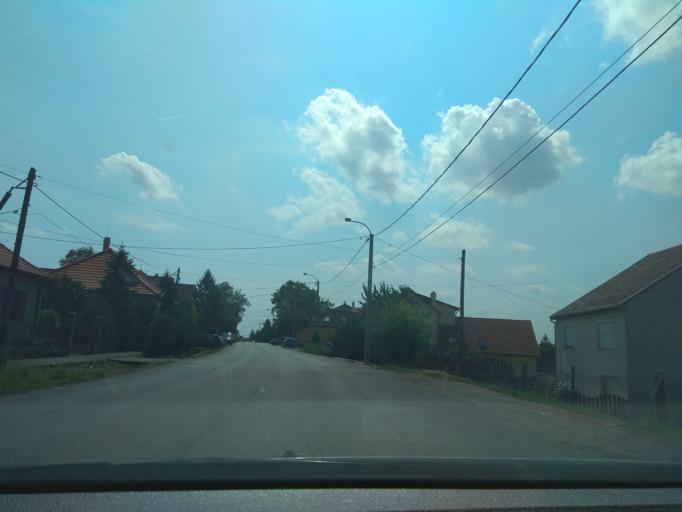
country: HU
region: Heves
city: Andornaktalya
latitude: 47.8624
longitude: 20.4067
